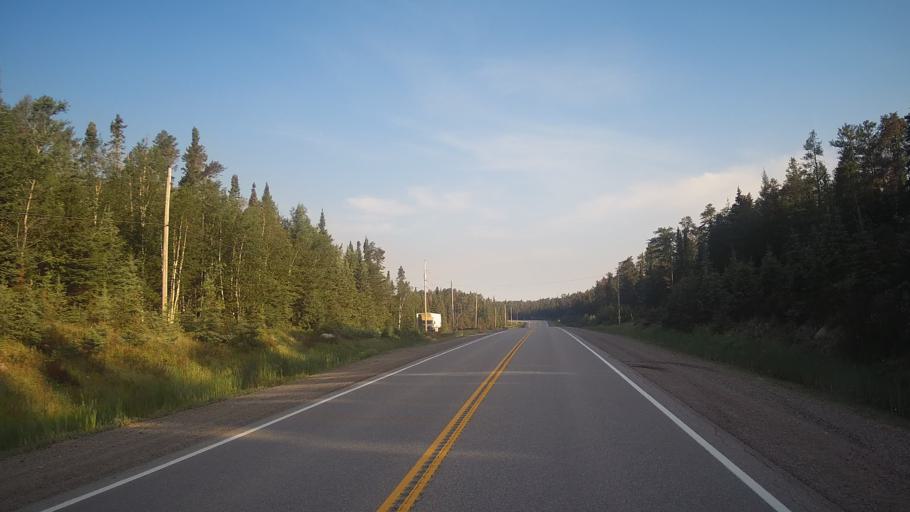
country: CA
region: Ontario
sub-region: Rainy River District
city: Atikokan
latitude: 49.3966
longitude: -91.6092
